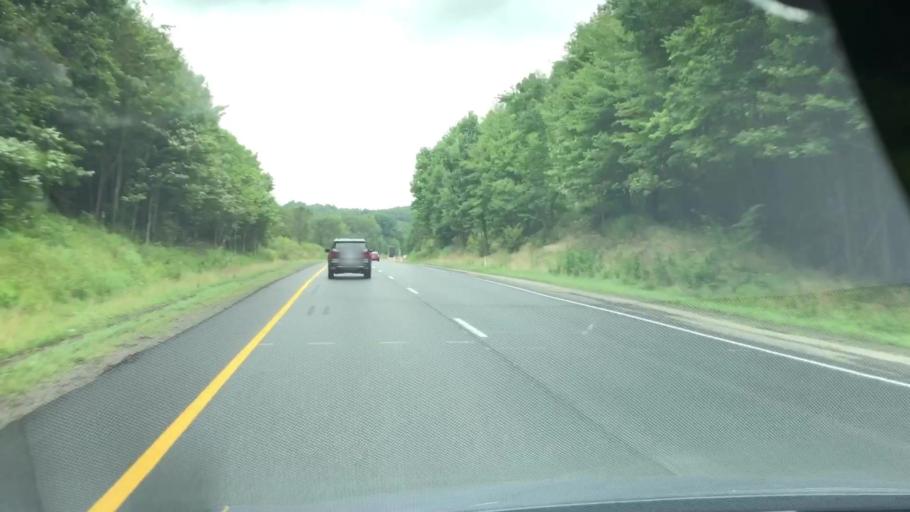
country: US
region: Pennsylvania
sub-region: Butler County
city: Prospect
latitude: 40.8962
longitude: -80.1218
